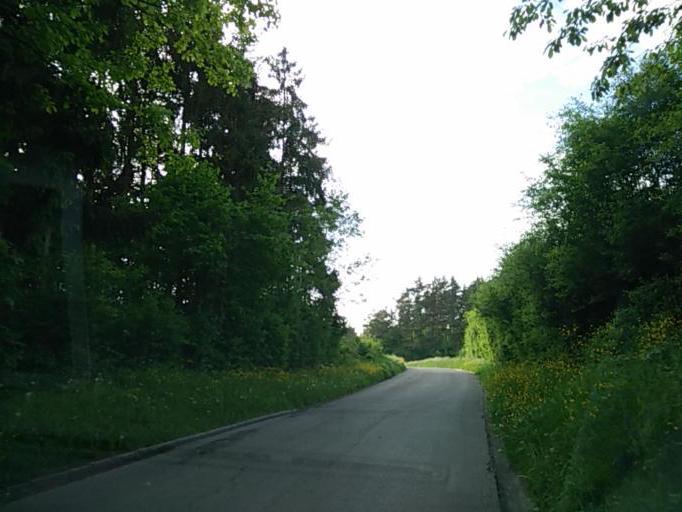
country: DE
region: Baden-Wuerttemberg
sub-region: Tuebingen Region
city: Hirrlingen
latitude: 48.4134
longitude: 8.8614
